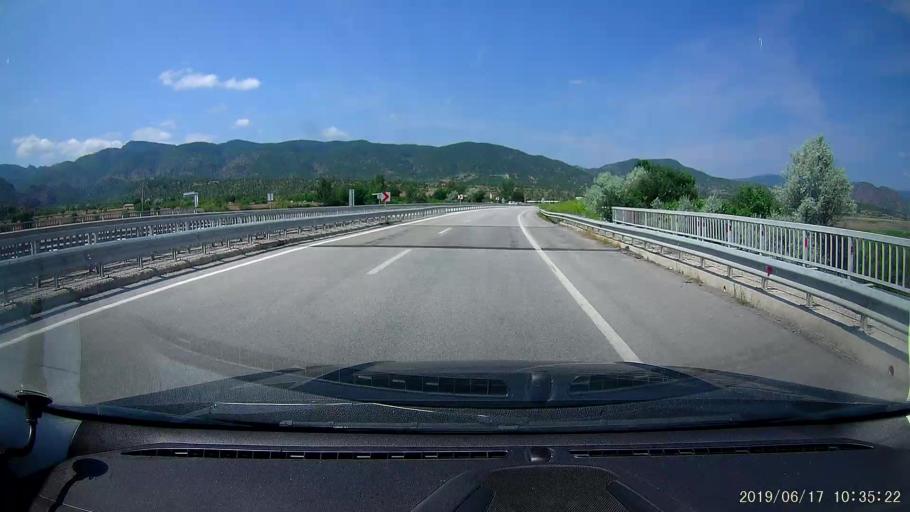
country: TR
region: Corum
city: Osmancik
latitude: 40.9732
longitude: 34.7055
